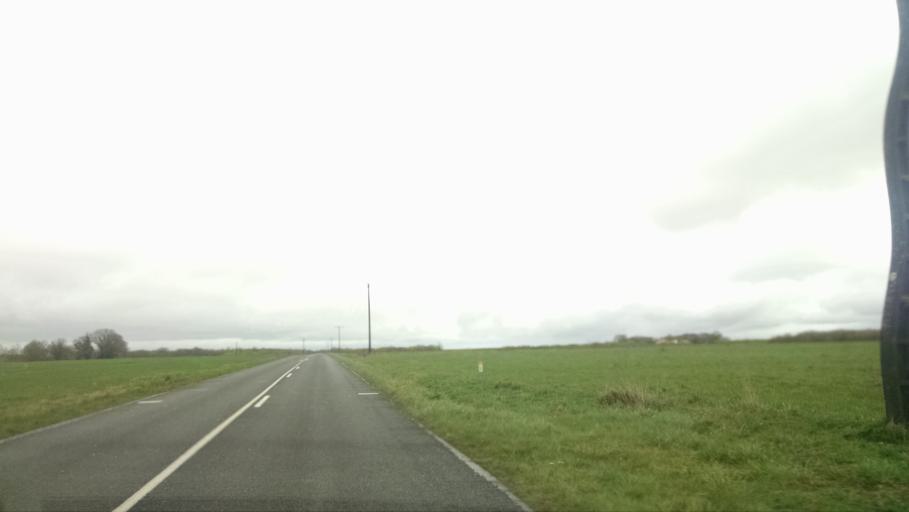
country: FR
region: Pays de la Loire
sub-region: Departement de la Loire-Atlantique
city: Maisdon-sur-Sevre
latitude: 47.1055
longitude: -1.3780
